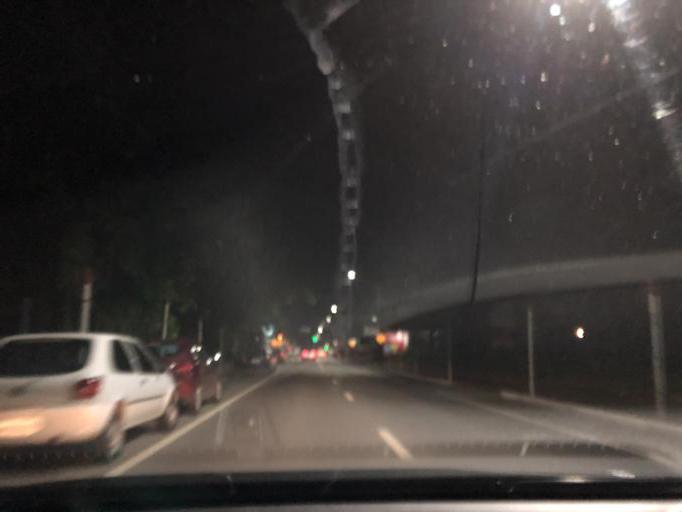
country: BR
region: Santa Catarina
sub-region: Jaragua Do Sul
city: Jaragua do Sul
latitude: -26.5148
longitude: -49.1226
